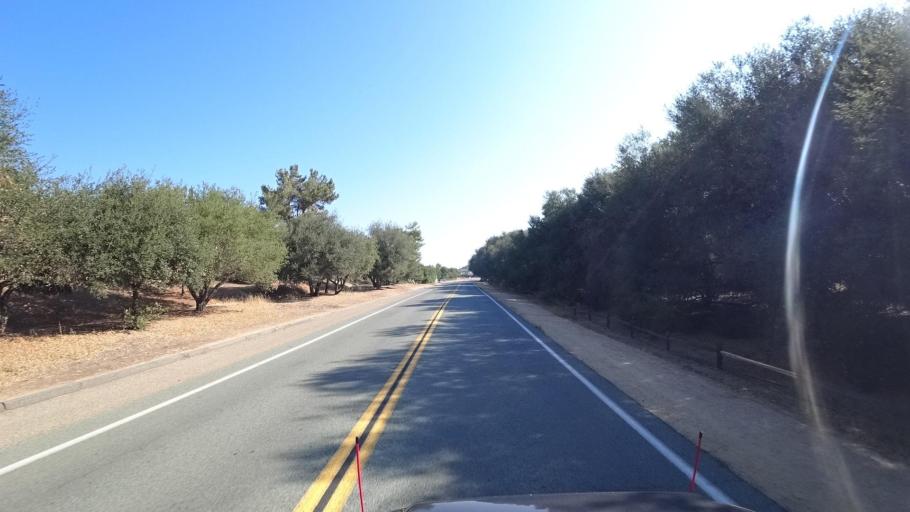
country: US
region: California
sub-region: San Diego County
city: Fallbrook
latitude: 33.3564
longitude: -117.2323
